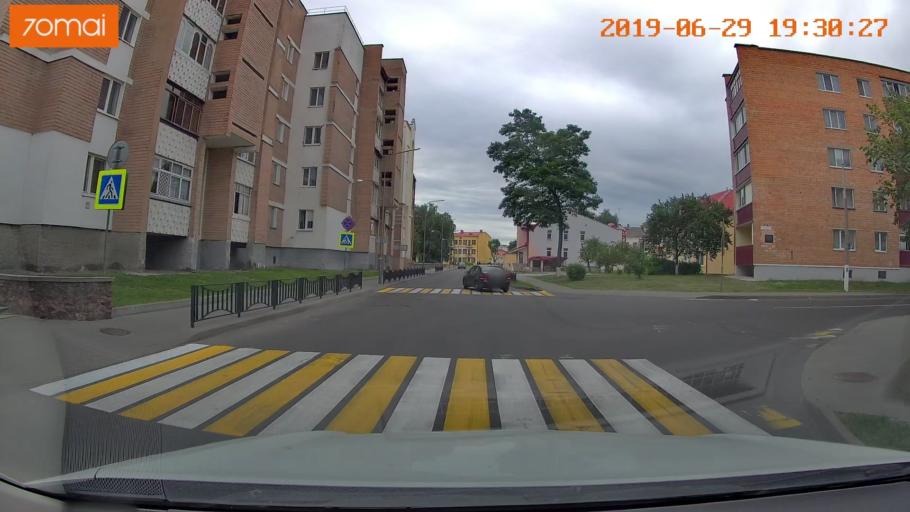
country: BY
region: Brest
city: Pinsk
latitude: 52.1155
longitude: 26.1117
